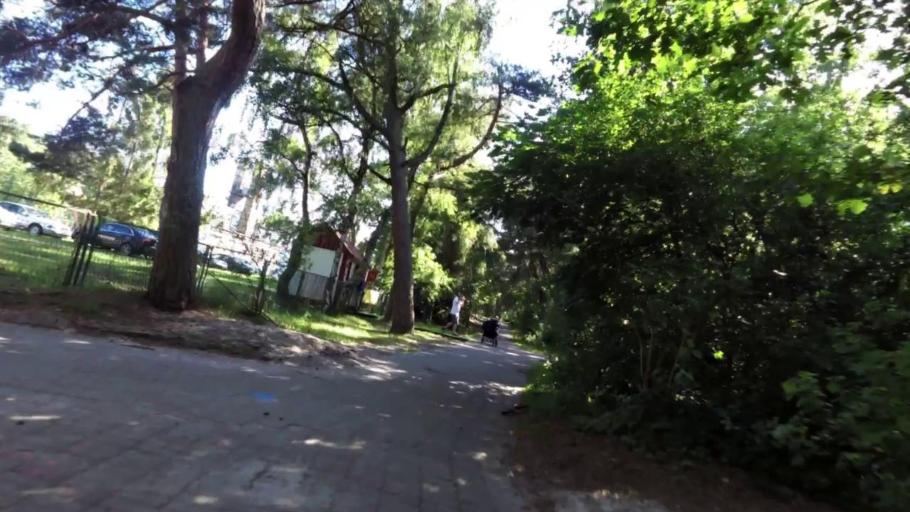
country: PL
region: West Pomeranian Voivodeship
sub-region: Powiat slawienski
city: Darlowo
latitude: 54.3780
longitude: 16.3099
